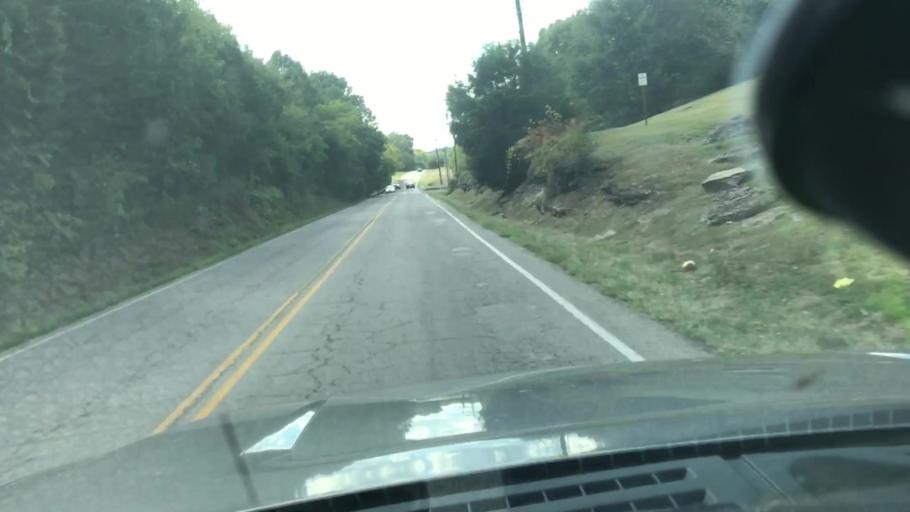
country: US
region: Tennessee
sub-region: Davidson County
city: Forest Hills
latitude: 36.0267
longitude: -86.9010
